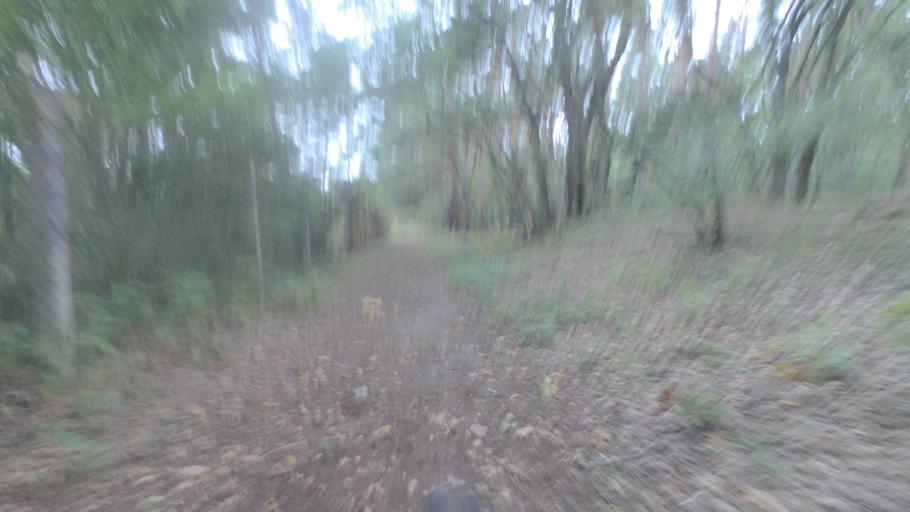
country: DE
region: Berlin
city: Berlin Koepenick
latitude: 52.4590
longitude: 13.5994
